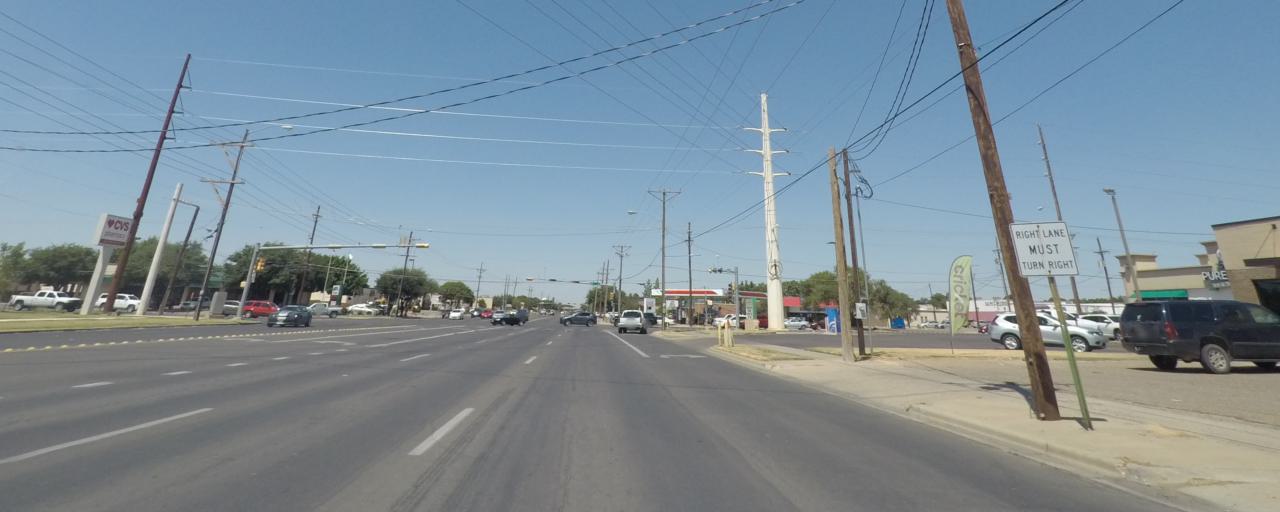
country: US
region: Texas
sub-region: Lubbock County
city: Lubbock
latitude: 33.5190
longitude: -101.8876
